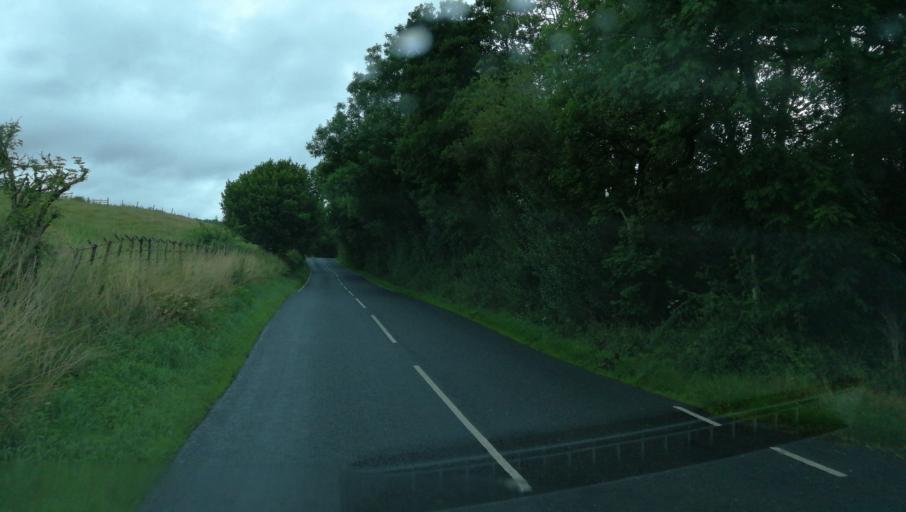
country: GB
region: England
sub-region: Cumbria
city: Penrith
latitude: 54.6262
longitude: -2.8128
